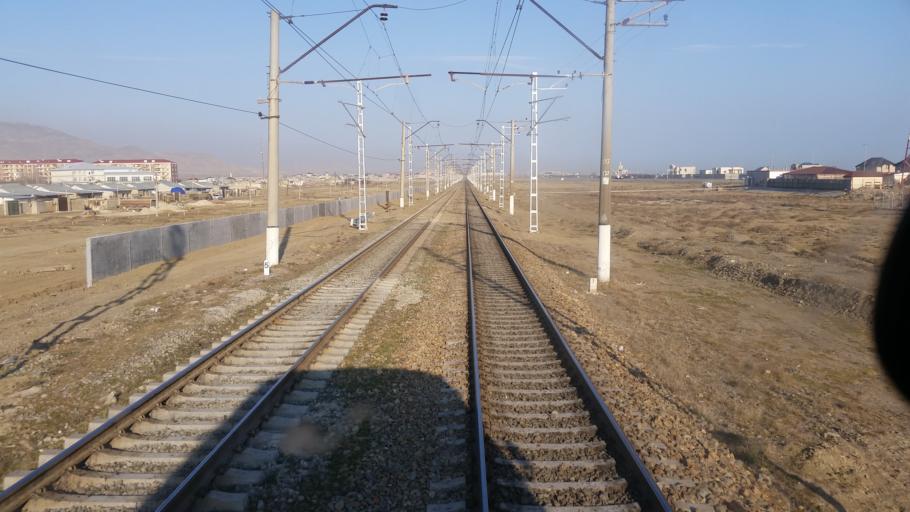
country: AZ
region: Baki
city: Qobustan
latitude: 40.1938
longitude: 49.5028
